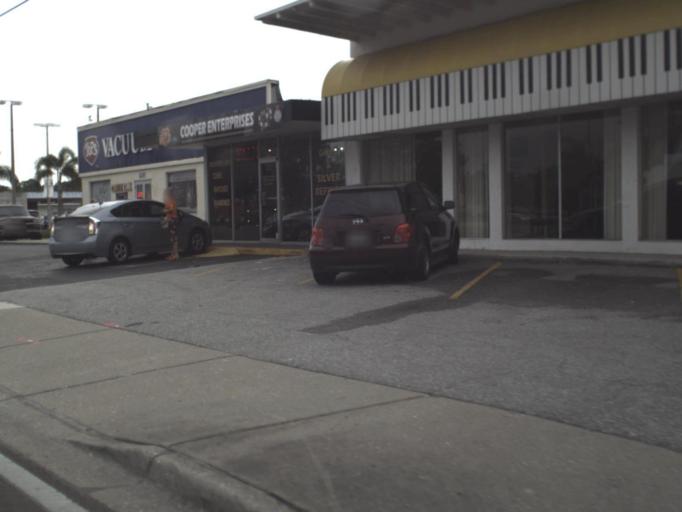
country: US
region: Florida
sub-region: Sarasota County
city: South Sarasota
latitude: 27.2988
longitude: -82.5278
